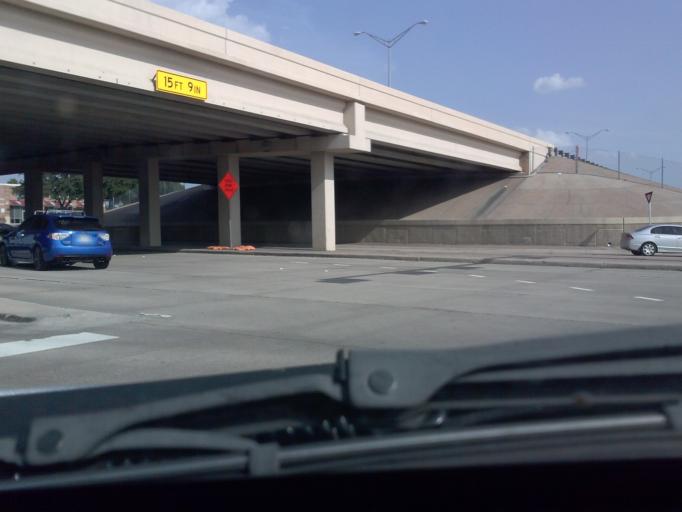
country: US
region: Texas
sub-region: Denton County
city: The Colony
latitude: 33.0453
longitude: -96.8300
